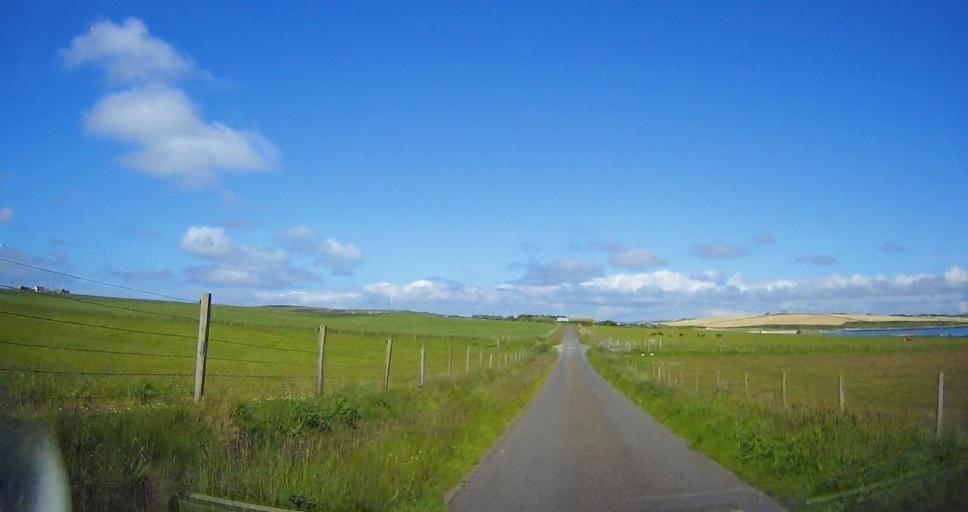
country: GB
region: Scotland
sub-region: Orkney Islands
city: Kirkwall
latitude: 58.8328
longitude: -2.8995
